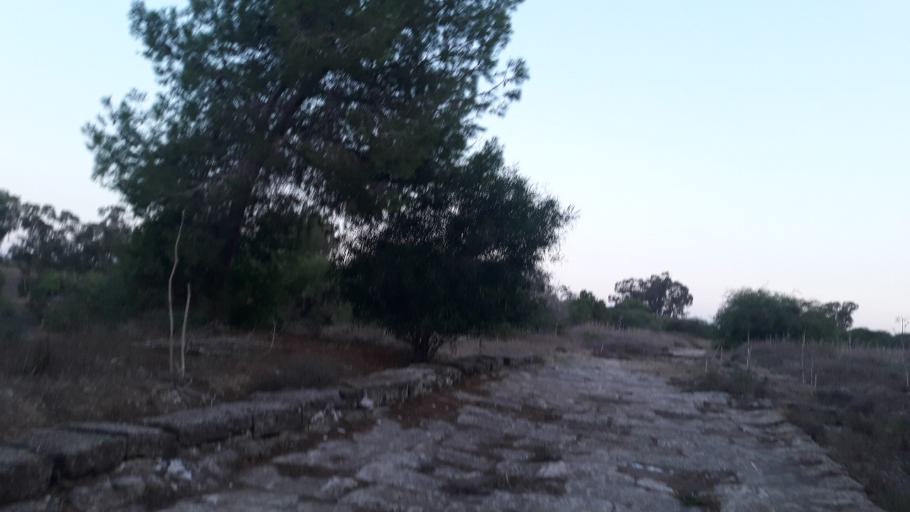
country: CY
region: Ammochostos
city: Famagusta
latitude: 35.1830
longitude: 33.9014
